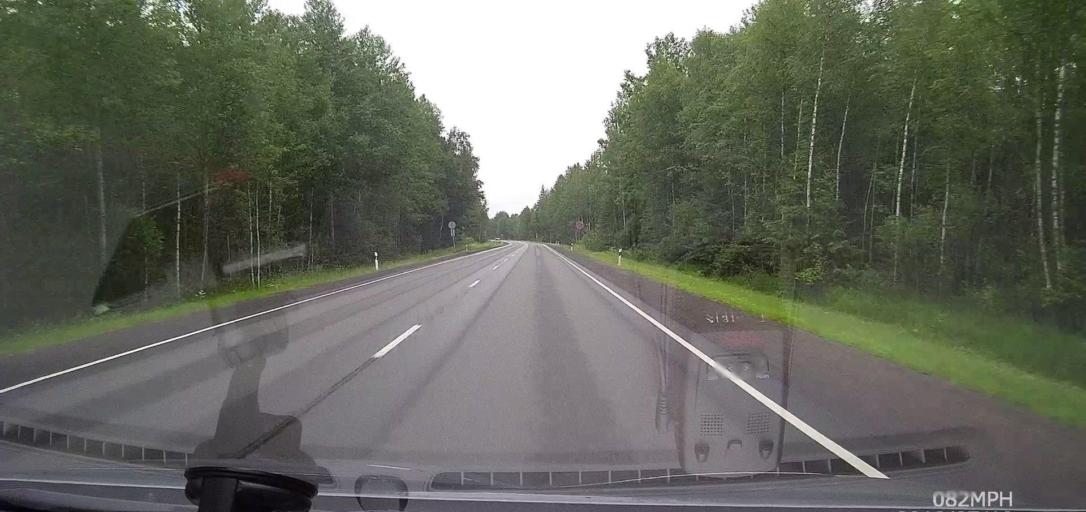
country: RU
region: Leningrad
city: Syas'stroy
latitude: 60.1814
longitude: 32.6301
